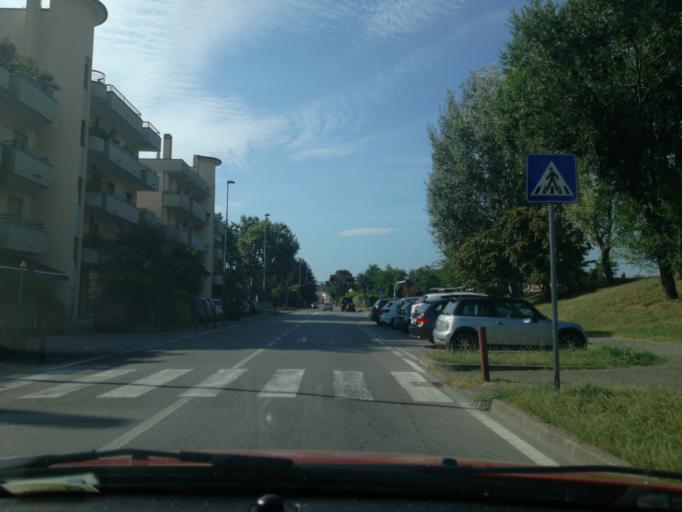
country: IT
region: Lombardy
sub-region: Provincia di Monza e Brianza
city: Arcore
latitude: 45.6346
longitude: 9.3383
